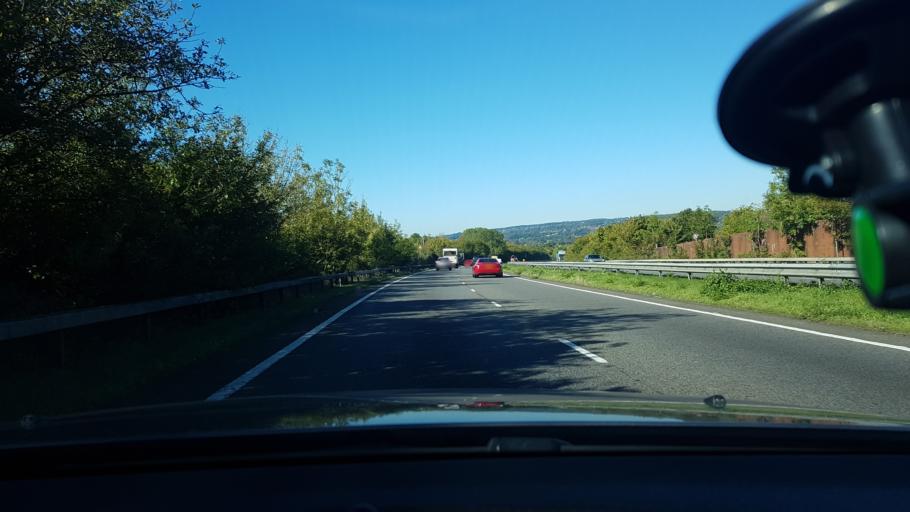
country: GB
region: England
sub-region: Surrey
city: Seale
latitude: 51.2253
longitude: -0.7263
